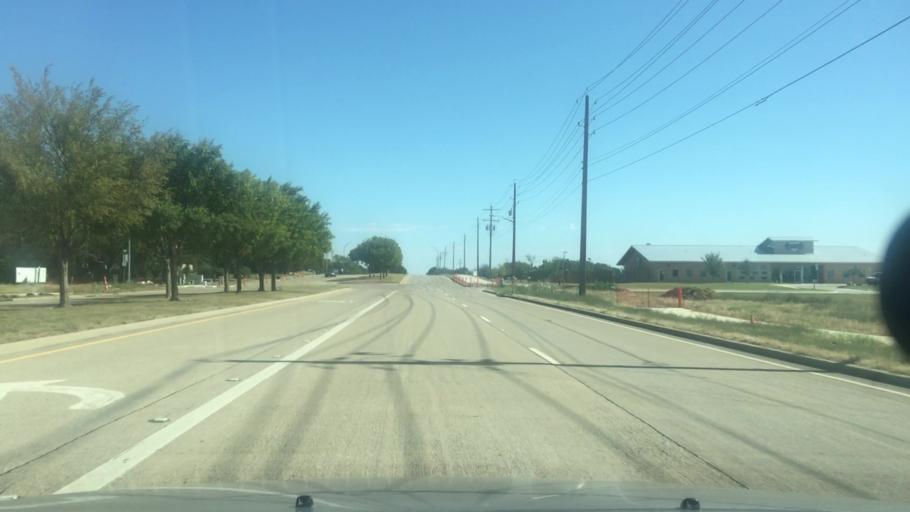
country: US
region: Texas
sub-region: Denton County
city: Denton
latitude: 33.2487
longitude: -97.1488
